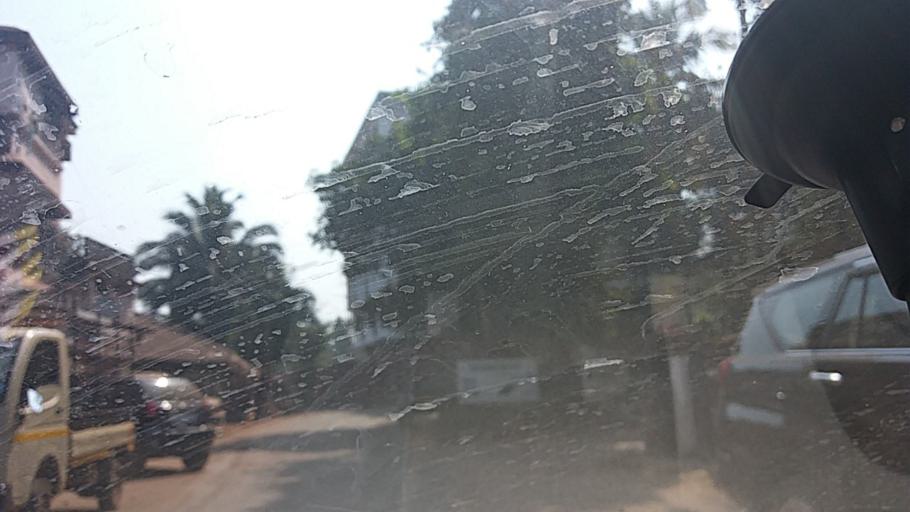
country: IN
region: Goa
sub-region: South Goa
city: Madgaon
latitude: 15.2885
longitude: 73.9537
